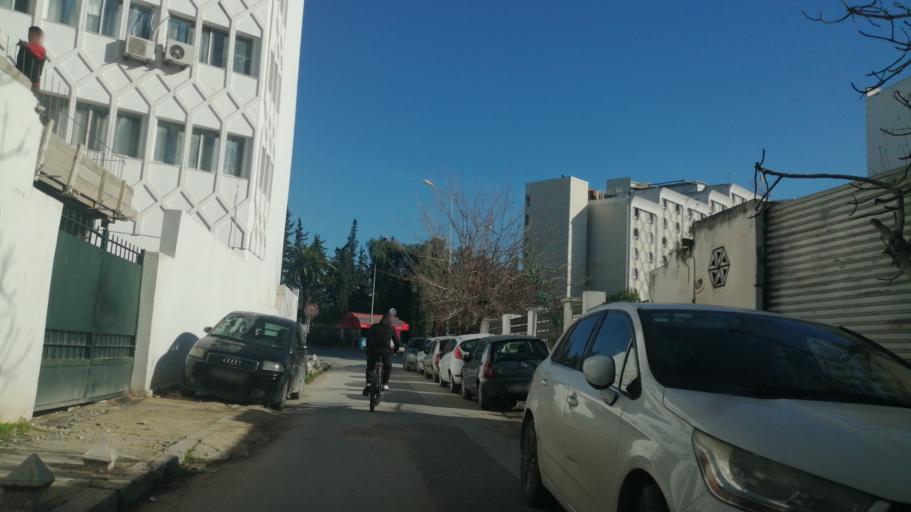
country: TN
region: Tunis
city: Tunis
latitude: 36.8130
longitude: 10.1721
